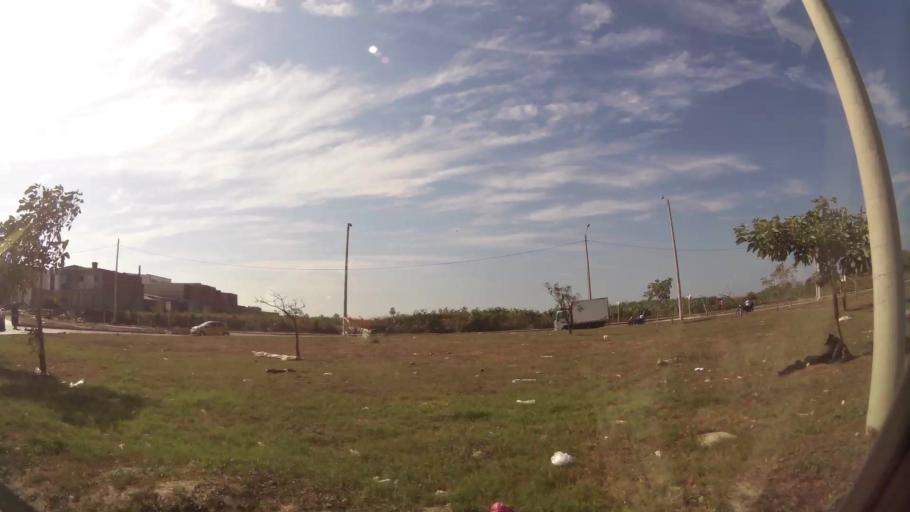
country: CO
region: Atlantico
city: Soledad
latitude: 10.9208
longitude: -74.8175
